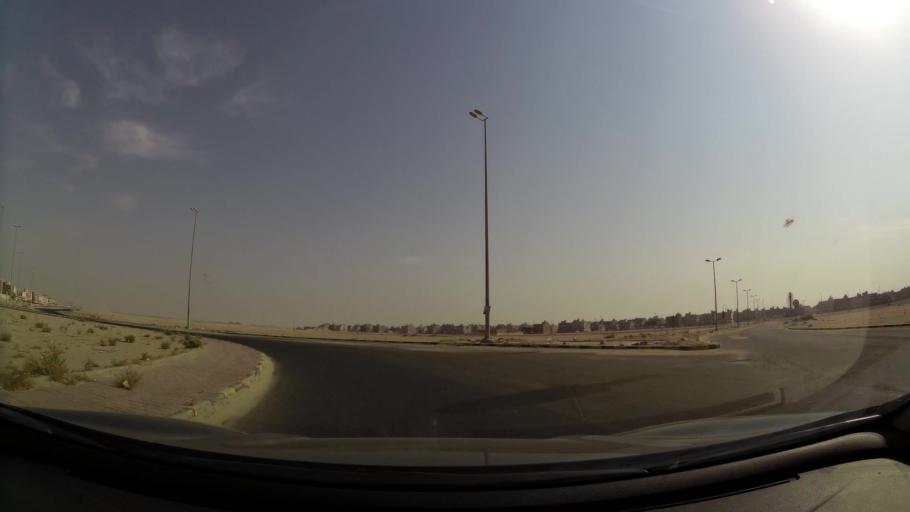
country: KW
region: Al Ahmadi
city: Al Wafrah
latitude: 28.7913
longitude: 48.0769
